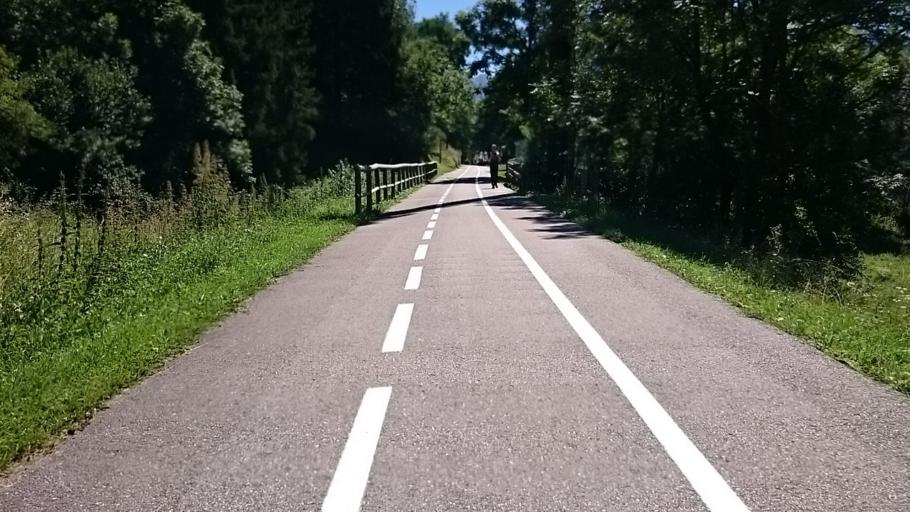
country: IT
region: Veneto
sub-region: Provincia di Belluno
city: Borca
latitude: 46.4396
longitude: 12.2177
